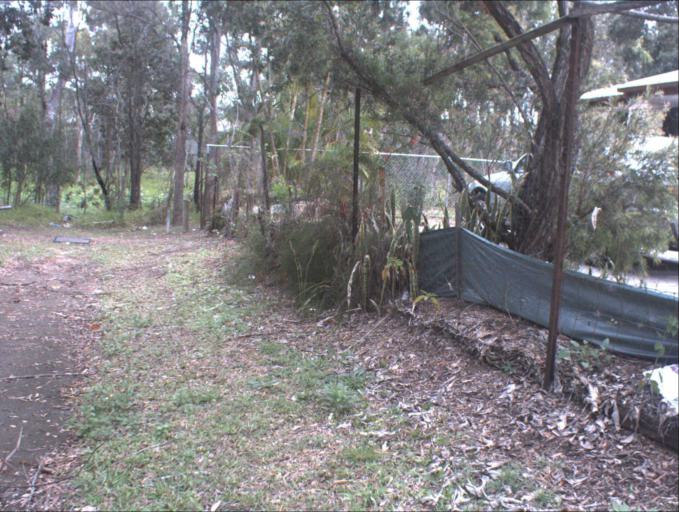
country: AU
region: Queensland
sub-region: Logan
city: Park Ridge South
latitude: -27.6912
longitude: 153.0207
